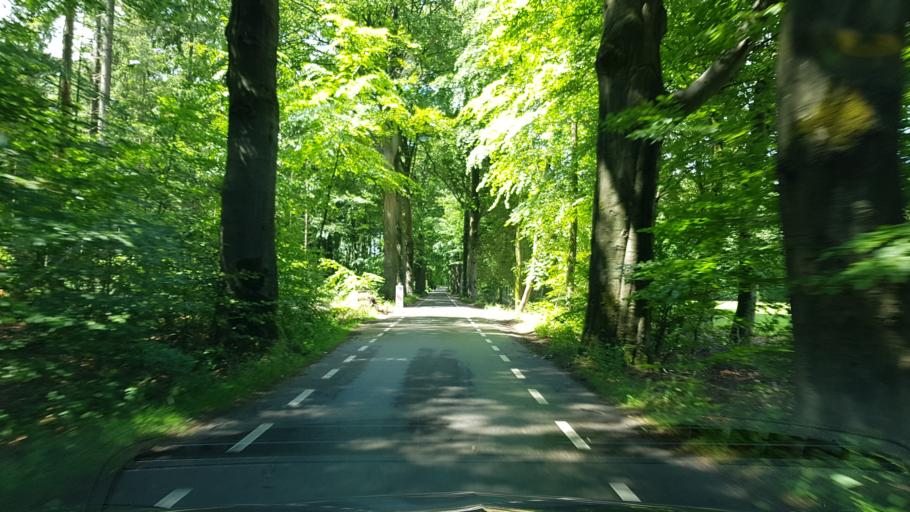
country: NL
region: Gelderland
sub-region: Gemeente Epe
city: Emst
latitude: 52.3465
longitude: 5.9253
